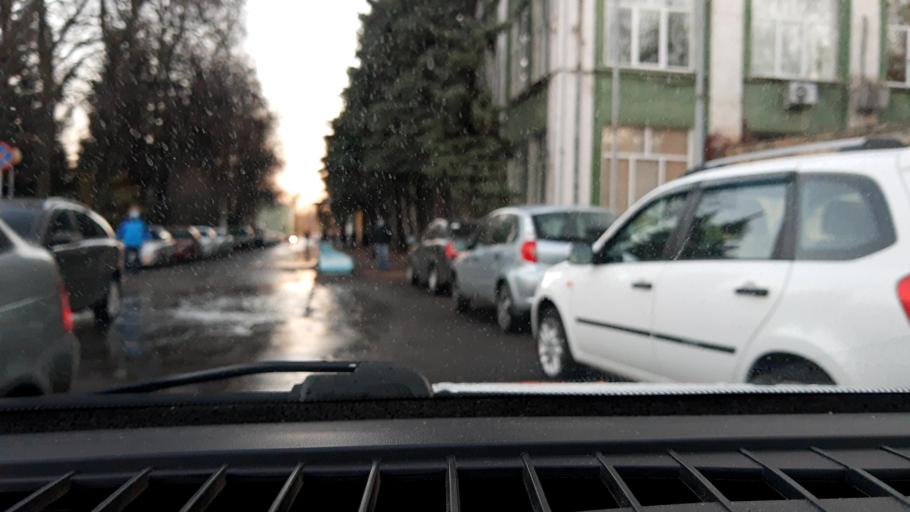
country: RU
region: Nizjnij Novgorod
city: Gorbatovka
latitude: 56.3277
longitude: 43.8580
